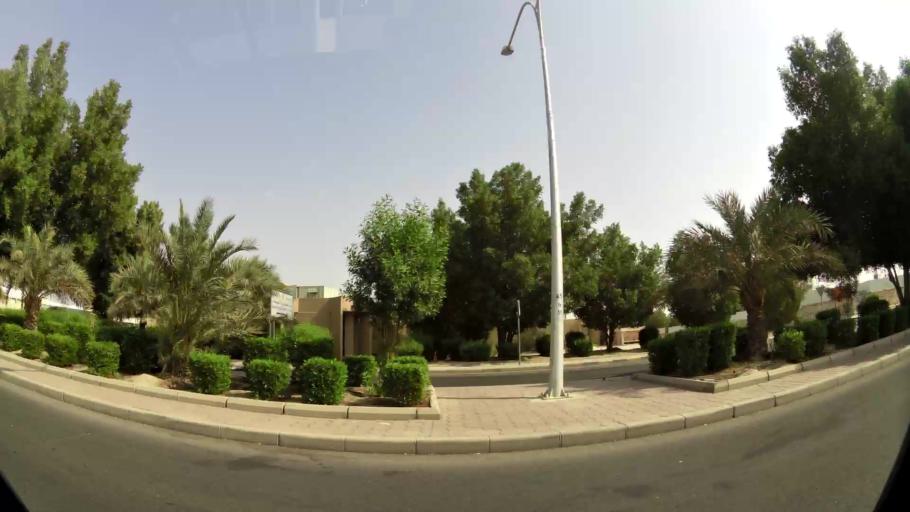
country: KW
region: Muhafazat al Jahra'
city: Al Jahra'
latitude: 29.3290
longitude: 47.6535
